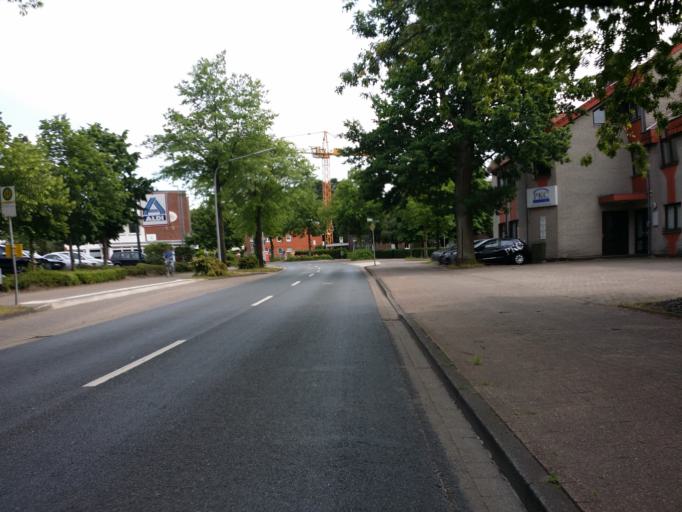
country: DE
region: Lower Saxony
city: Oldenburg
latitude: 53.1639
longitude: 8.2170
